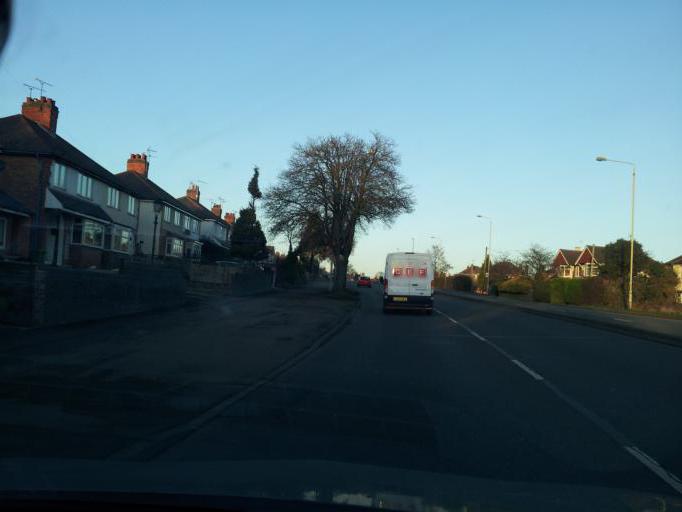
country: GB
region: England
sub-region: Leicestershire
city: Narborough
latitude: 52.5785
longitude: -1.1966
